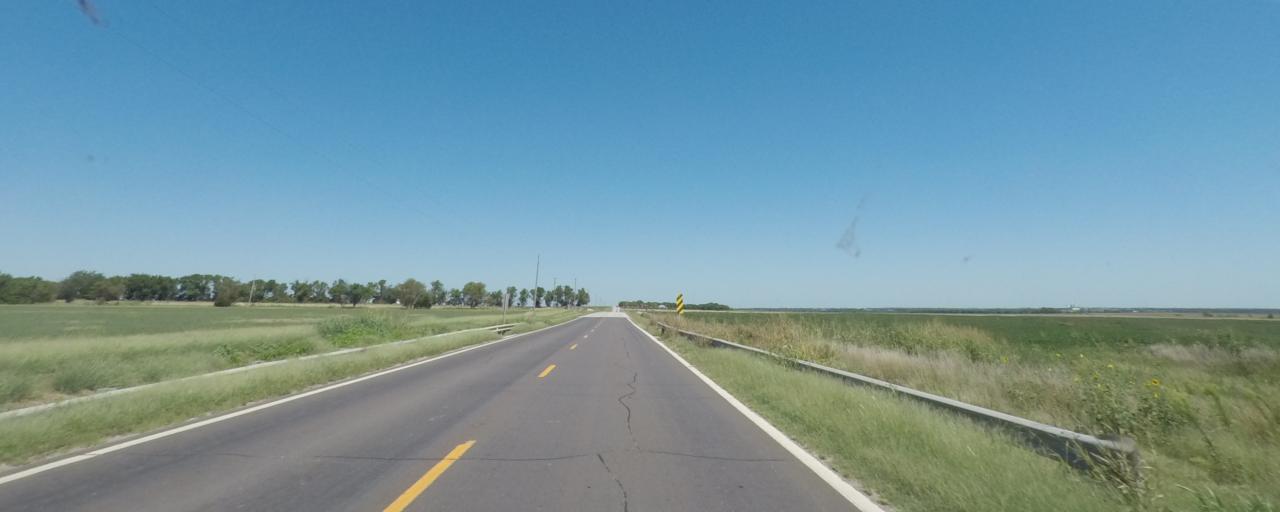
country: US
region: Kansas
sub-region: Sumner County
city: Wellington
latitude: 37.2066
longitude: -97.4023
